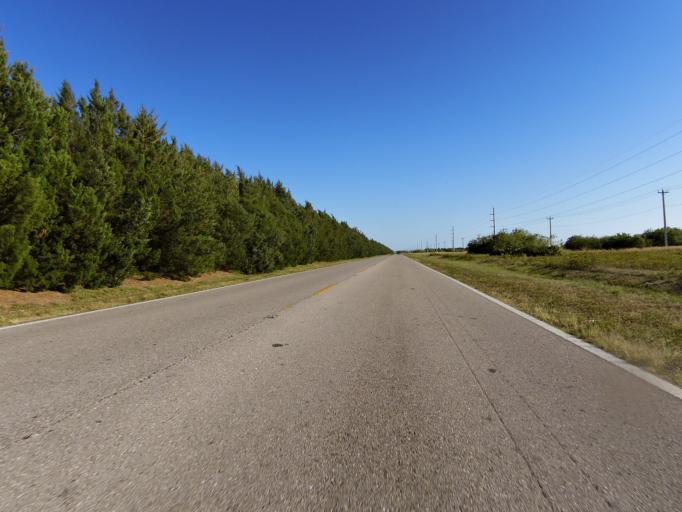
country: US
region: Florida
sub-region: Collier County
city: Immokalee
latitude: 26.3485
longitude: -81.4168
